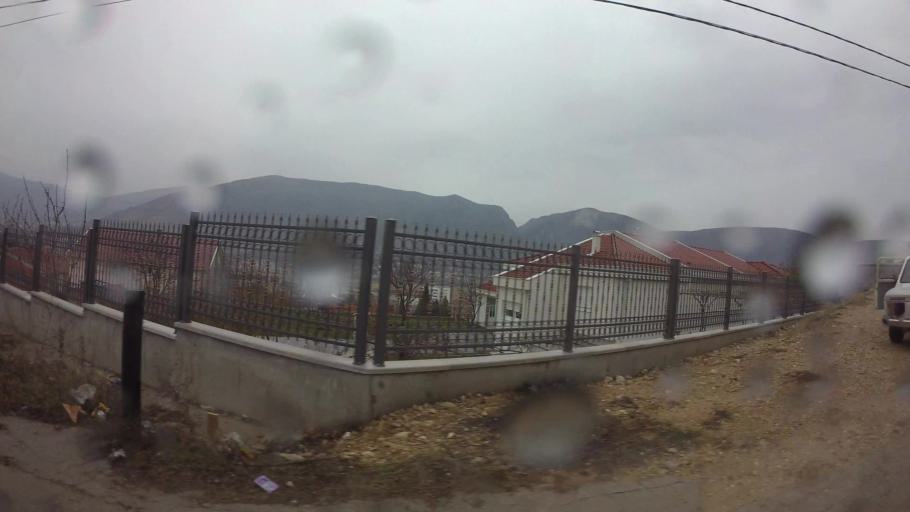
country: BA
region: Federation of Bosnia and Herzegovina
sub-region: Hercegovacko-Bosanski Kanton
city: Mostar
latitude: 43.3534
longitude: 17.8168
